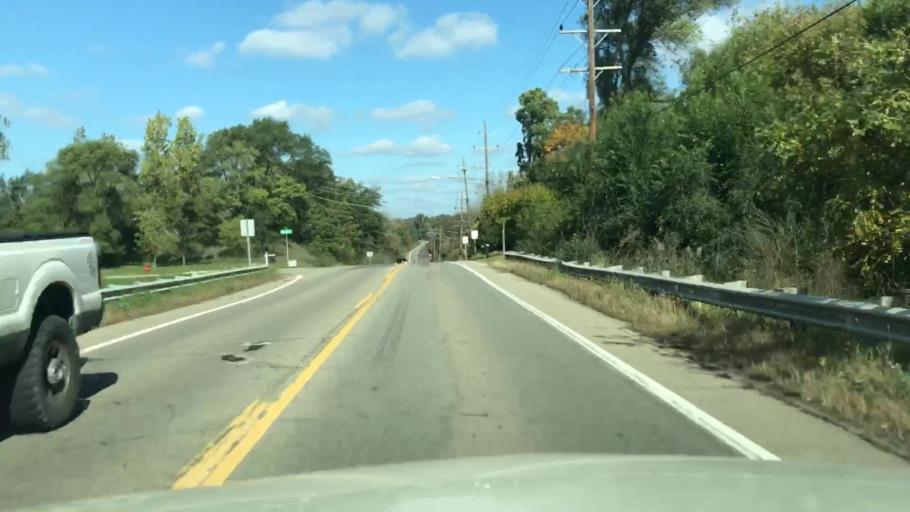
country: US
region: Michigan
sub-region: Oakland County
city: Rochester
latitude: 42.6593
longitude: -83.0930
